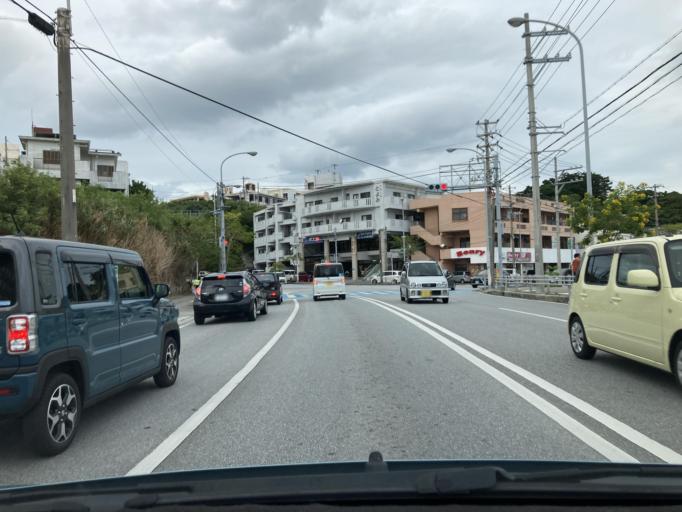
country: JP
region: Okinawa
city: Tomigusuku
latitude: 26.1813
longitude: 127.6811
